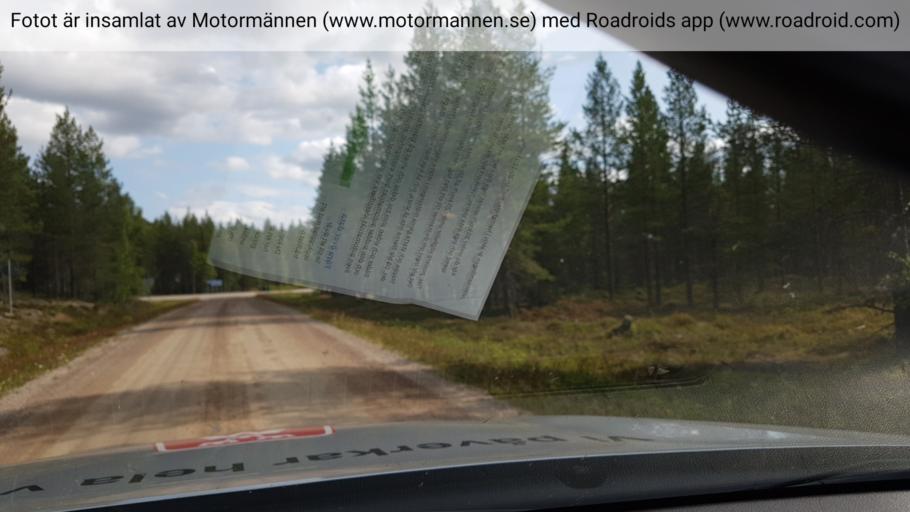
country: SE
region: Vaesterbotten
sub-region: Skelleftea Kommun
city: Boliden
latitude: 65.2038
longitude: 20.1997
